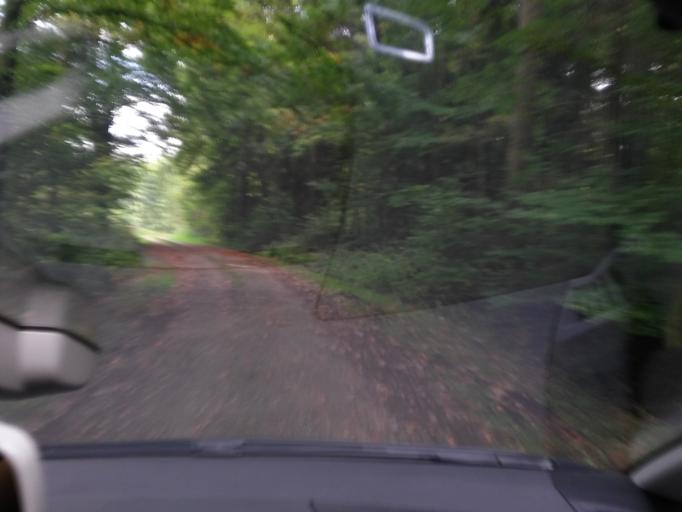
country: BE
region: Wallonia
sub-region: Province du Luxembourg
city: Attert
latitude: 49.7089
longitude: 5.7625
